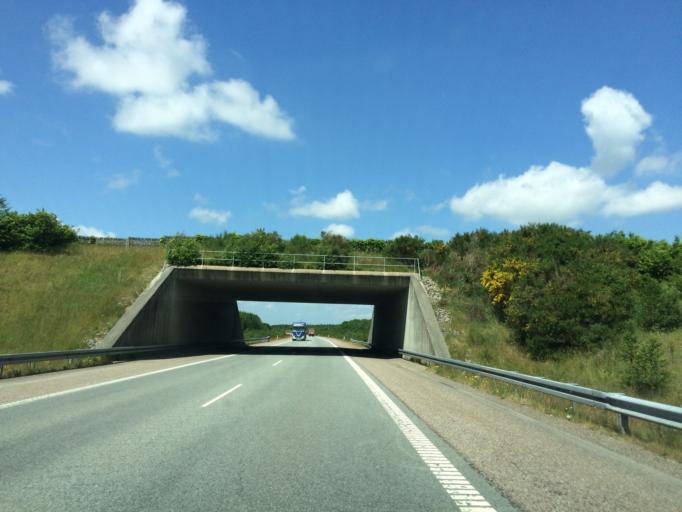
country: DK
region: Central Jutland
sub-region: Herning Kommune
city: Herning
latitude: 56.1773
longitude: 8.9830
